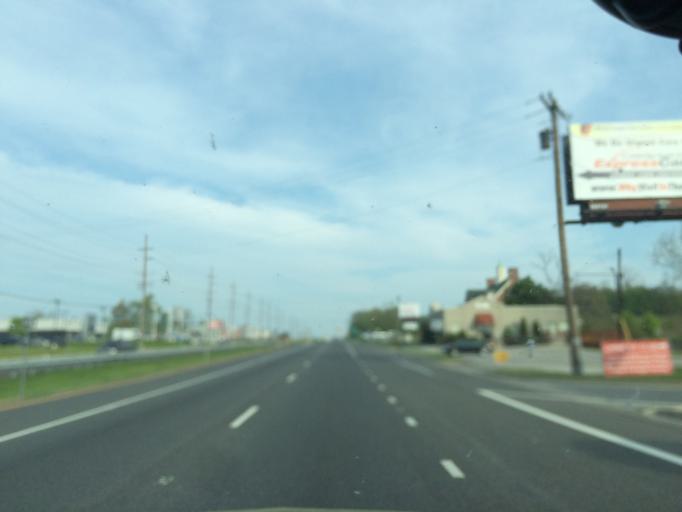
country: US
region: Maryland
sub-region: Carroll County
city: Westminster
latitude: 39.5559
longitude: -76.9600
